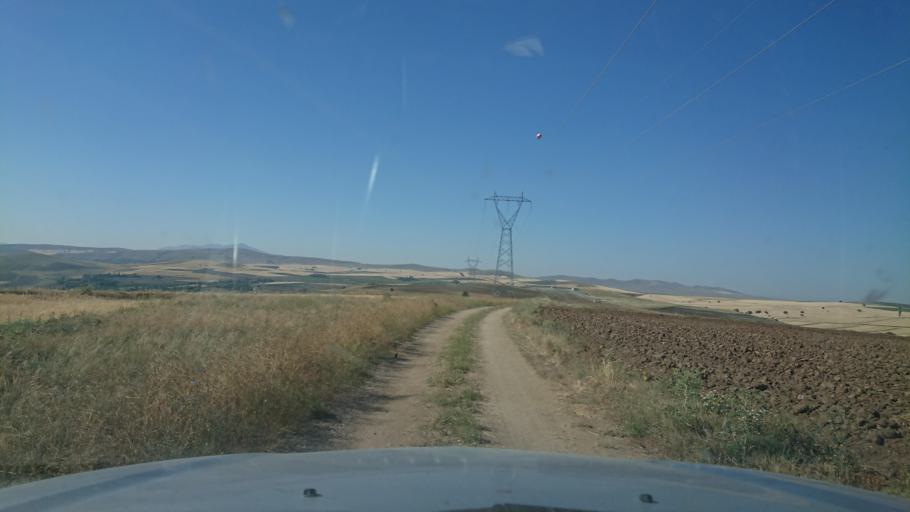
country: TR
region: Aksaray
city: Agacoren
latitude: 38.8354
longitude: 33.9456
